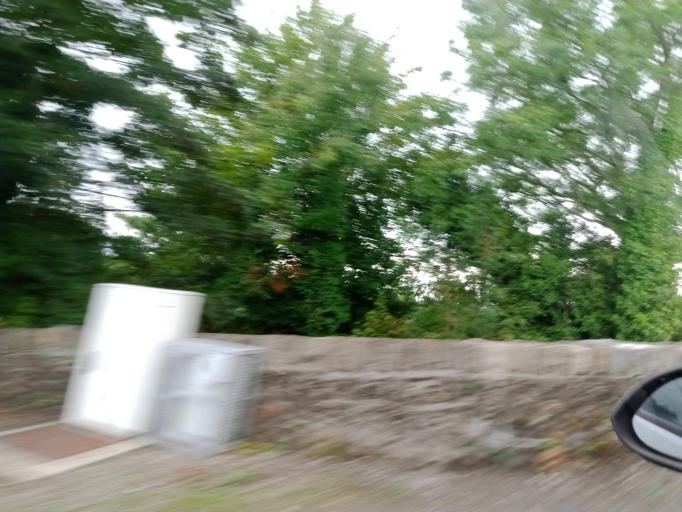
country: IE
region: Leinster
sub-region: Laois
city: Mountmellick
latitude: 53.1080
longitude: -7.3418
